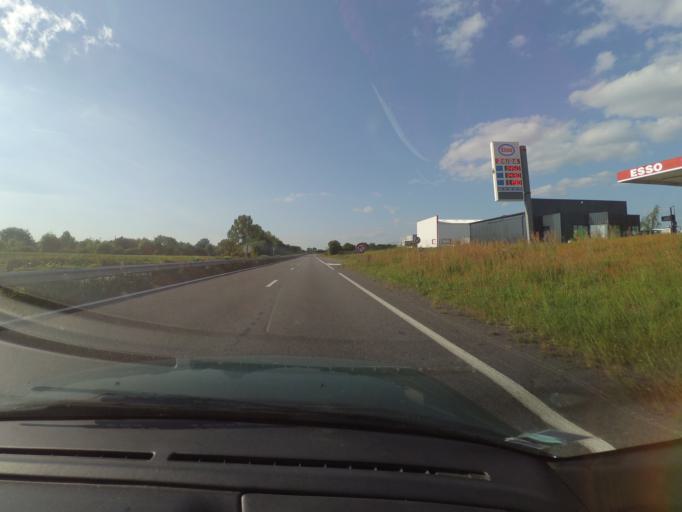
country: FR
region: Pays de la Loire
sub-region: Departement de la Vendee
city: Saligny
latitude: 46.8010
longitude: -1.4314
